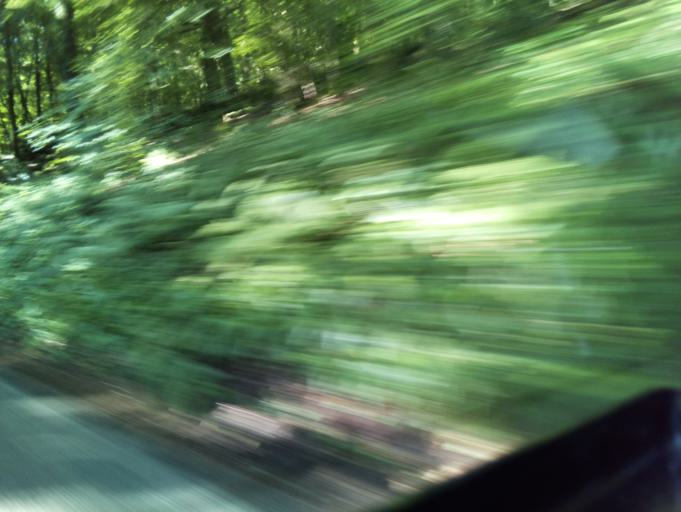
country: GB
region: Wales
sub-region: Monmouthshire
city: Tintern
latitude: 51.7284
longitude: -2.6890
